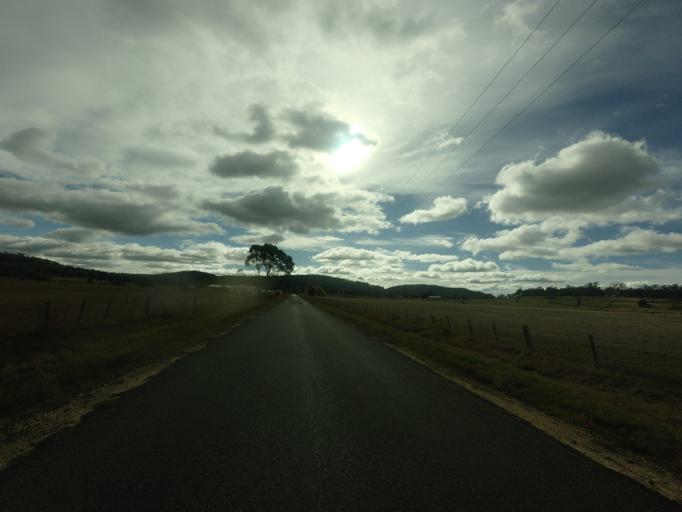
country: AU
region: Tasmania
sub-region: Brighton
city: Bridgewater
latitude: -42.4046
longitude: 147.3932
